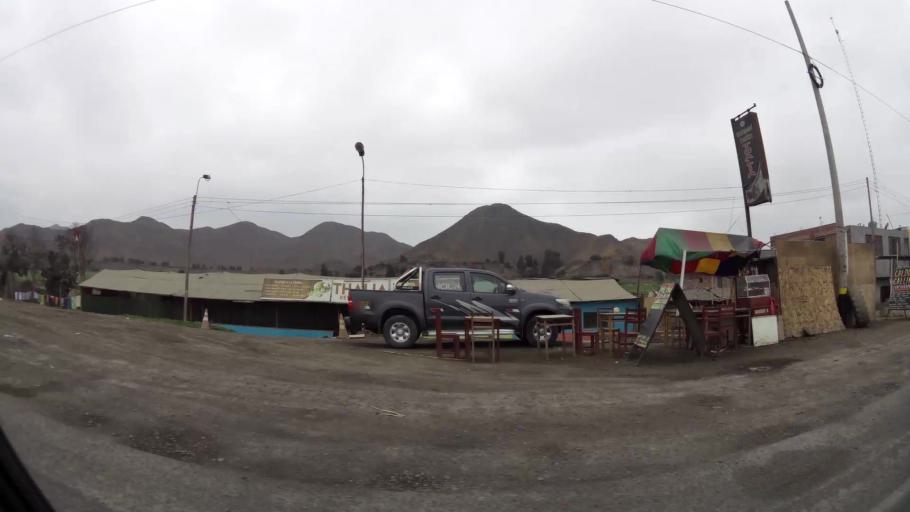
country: PE
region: Lima
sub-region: Barranca
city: Pativilca
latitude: -10.6694
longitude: -77.7942
